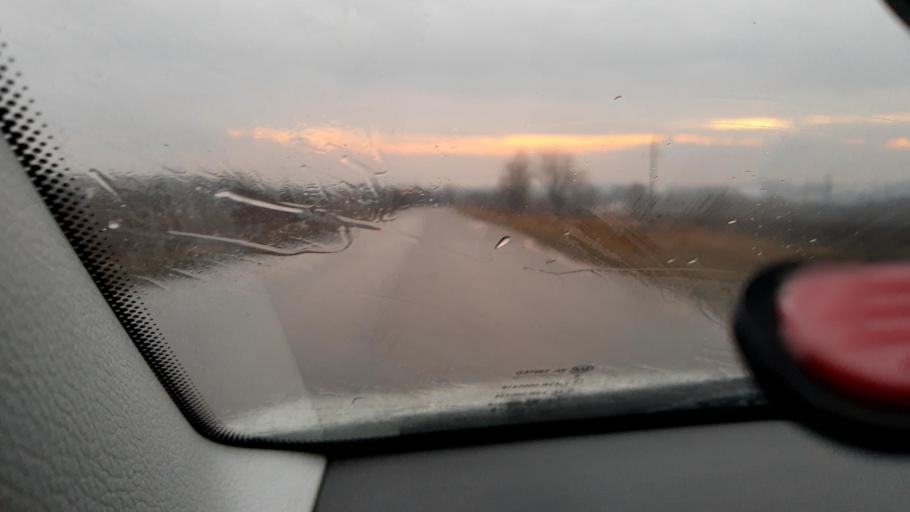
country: RU
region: Bashkortostan
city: Blagoveshchensk
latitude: 54.8902
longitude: 56.1461
